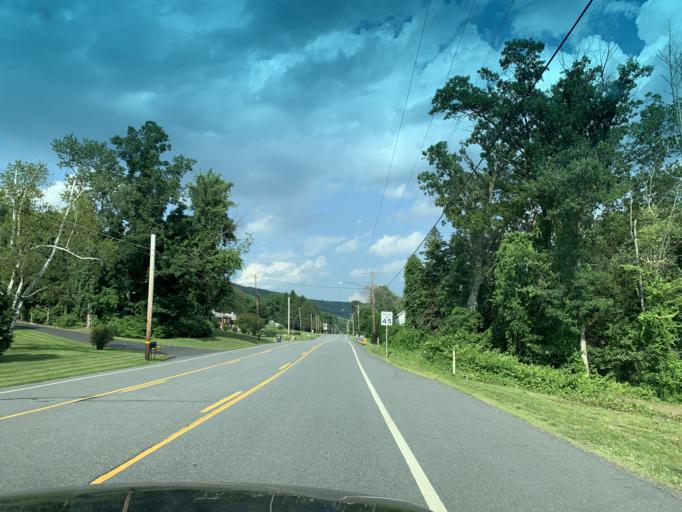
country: US
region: Pennsylvania
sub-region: Schuylkill County
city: Girardville
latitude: 40.7750
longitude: -76.3106
